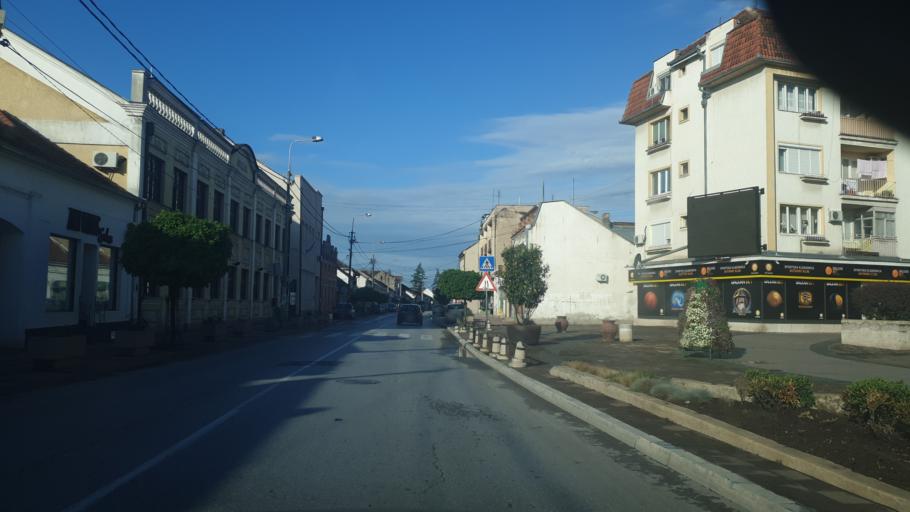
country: RS
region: Central Serbia
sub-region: Belgrade
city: Obrenovac
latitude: 44.6540
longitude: 20.2028
